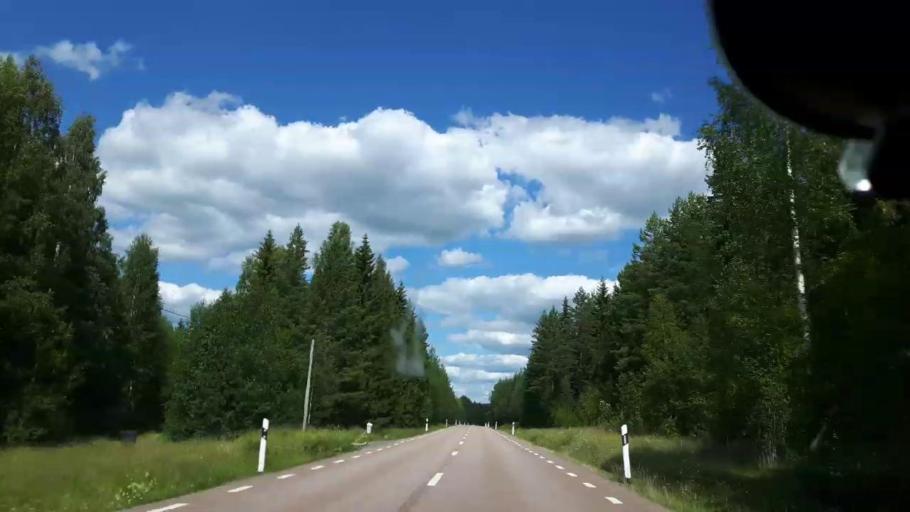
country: SE
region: Jaemtland
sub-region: Ragunda Kommun
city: Hammarstrand
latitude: 62.9095
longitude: 16.7022
